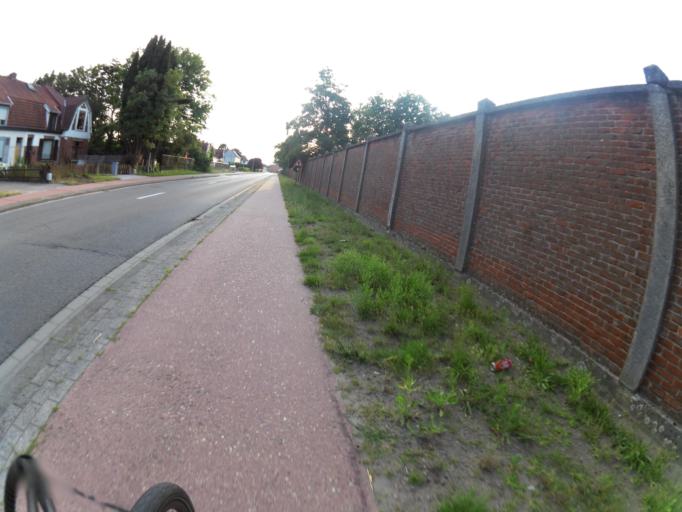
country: BE
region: Flanders
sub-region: Provincie Antwerpen
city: Balen
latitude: 51.1925
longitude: 5.1650
